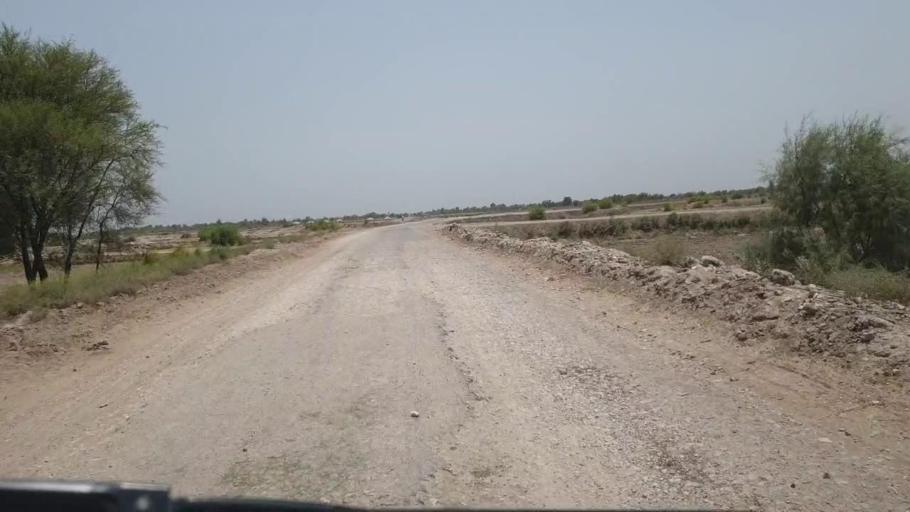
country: PK
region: Sindh
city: Daulatpur
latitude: 26.4575
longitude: 68.1186
